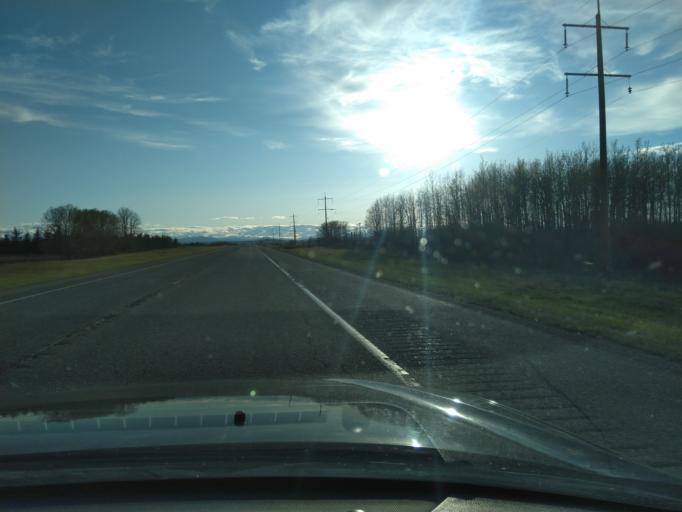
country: CA
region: Alberta
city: Cochrane
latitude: 51.0234
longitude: -114.3595
